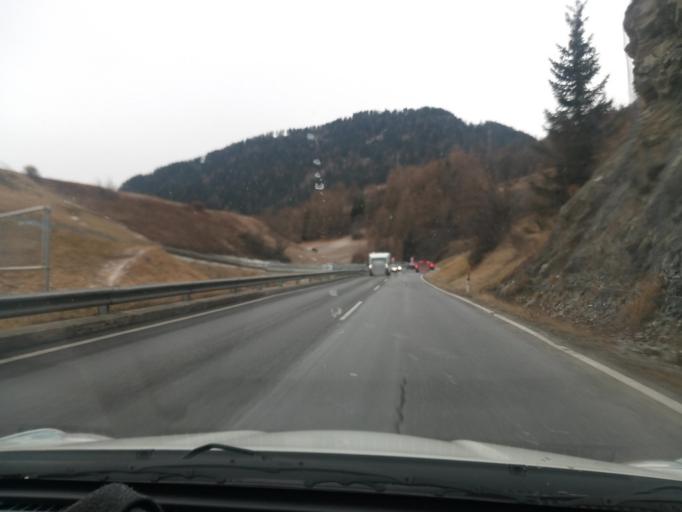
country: AT
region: Tyrol
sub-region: Politischer Bezirk Landeck
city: Nauders
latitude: 46.8985
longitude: 10.4939
